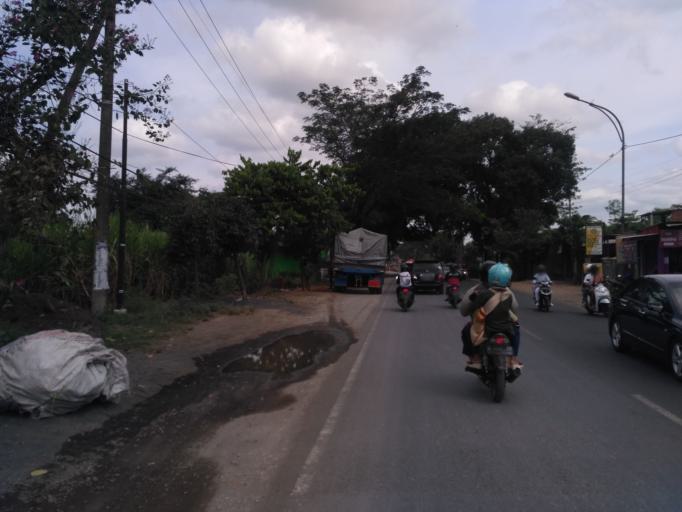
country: ID
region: East Java
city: Kebonsari
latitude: -8.0290
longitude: 112.6272
